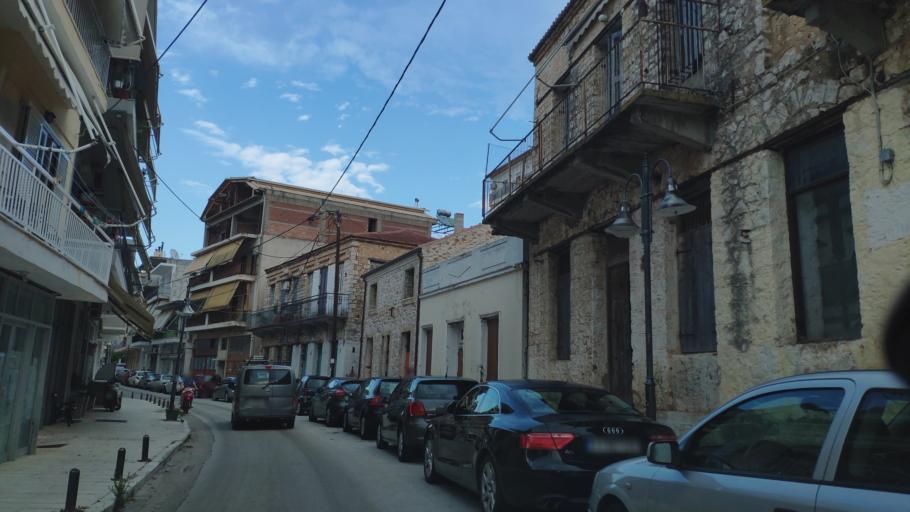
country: GR
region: West Greece
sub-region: Nomos Aitolias kai Akarnanias
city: Amfilochia
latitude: 38.8646
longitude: 21.1708
